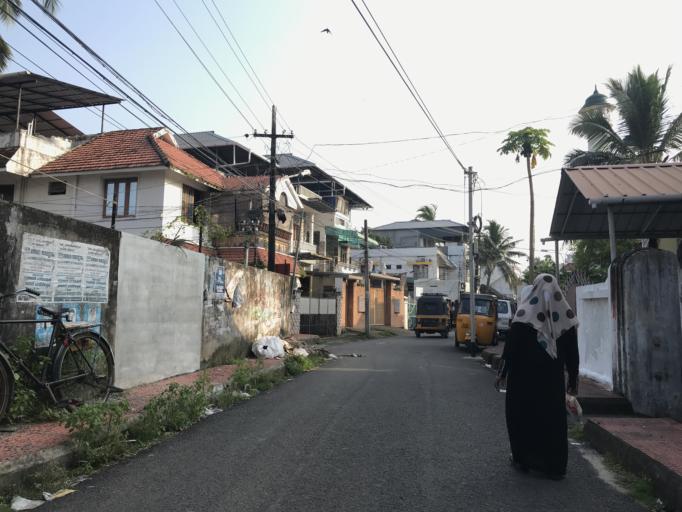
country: IN
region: Kerala
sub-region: Ernakulam
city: Cochin
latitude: 9.9648
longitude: 76.2478
